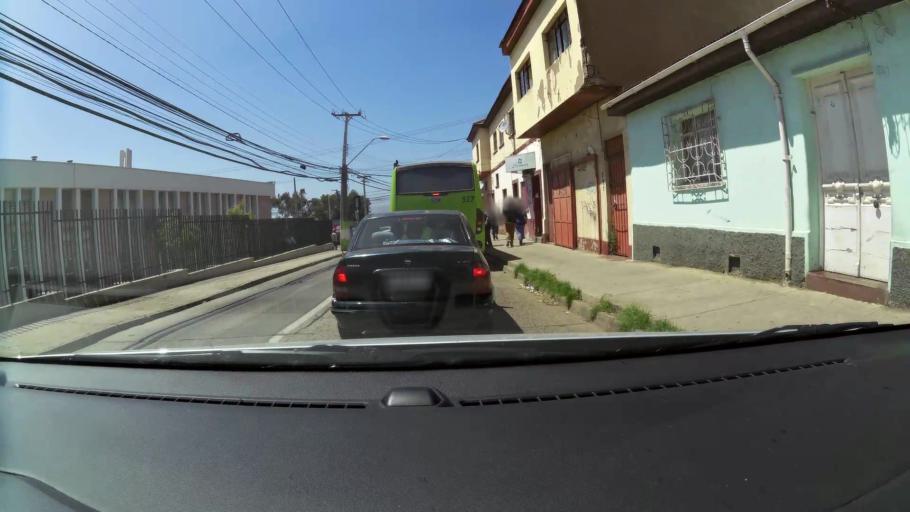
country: CL
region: Valparaiso
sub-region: Provincia de Valparaiso
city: Valparaiso
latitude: -33.0363
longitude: -71.6444
